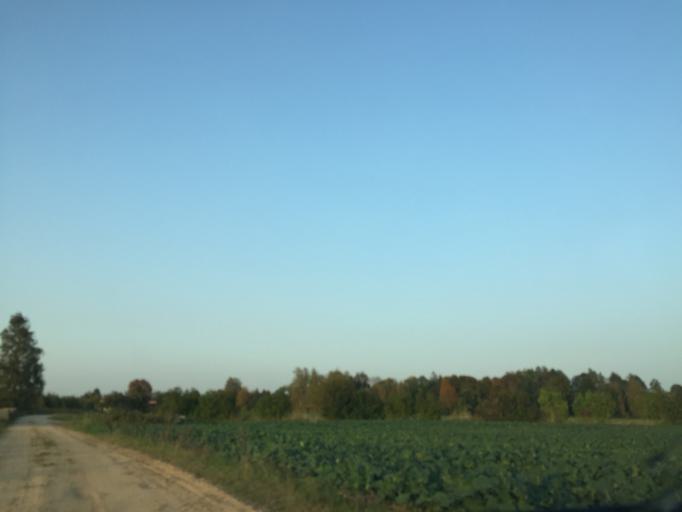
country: LV
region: Lielvarde
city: Lielvarde
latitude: 56.7918
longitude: 24.8186
